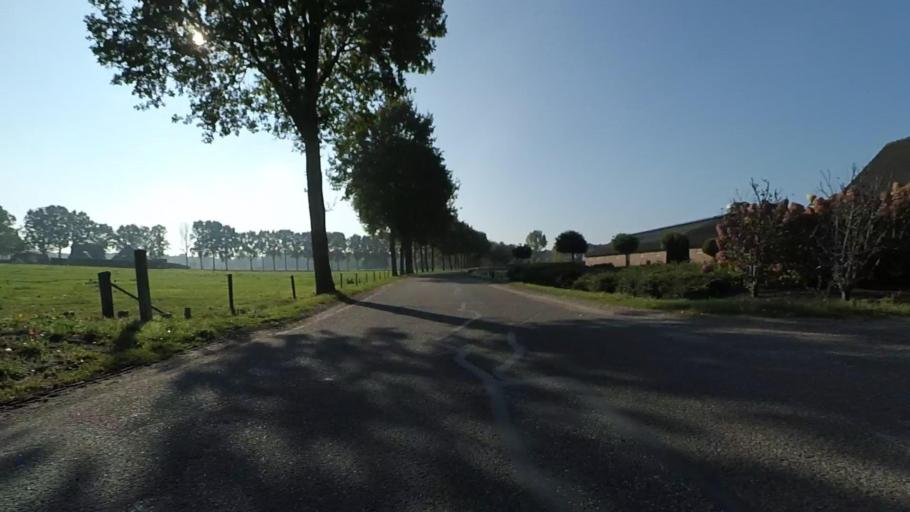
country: NL
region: Gelderland
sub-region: Gemeente Putten
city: Putten
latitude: 52.2391
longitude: 5.5544
